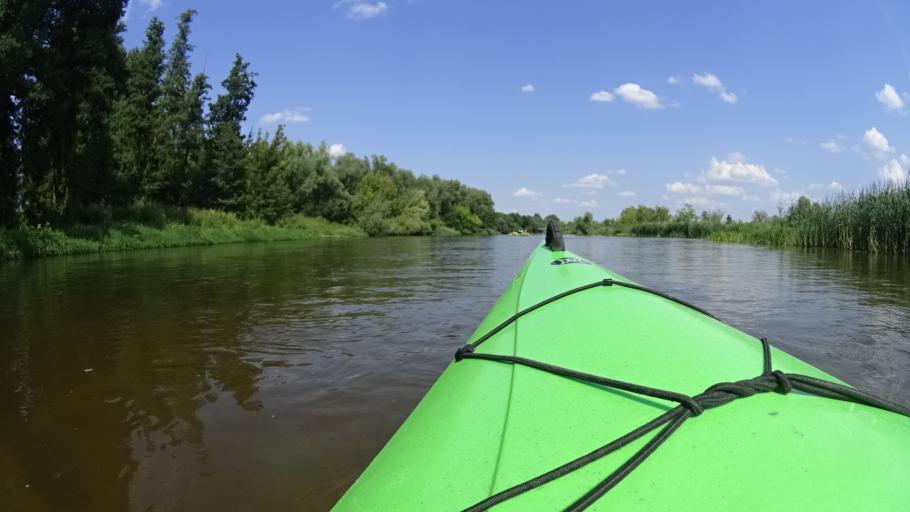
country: PL
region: Masovian Voivodeship
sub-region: Powiat bialobrzeski
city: Wysmierzyce
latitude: 51.6603
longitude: 20.8594
